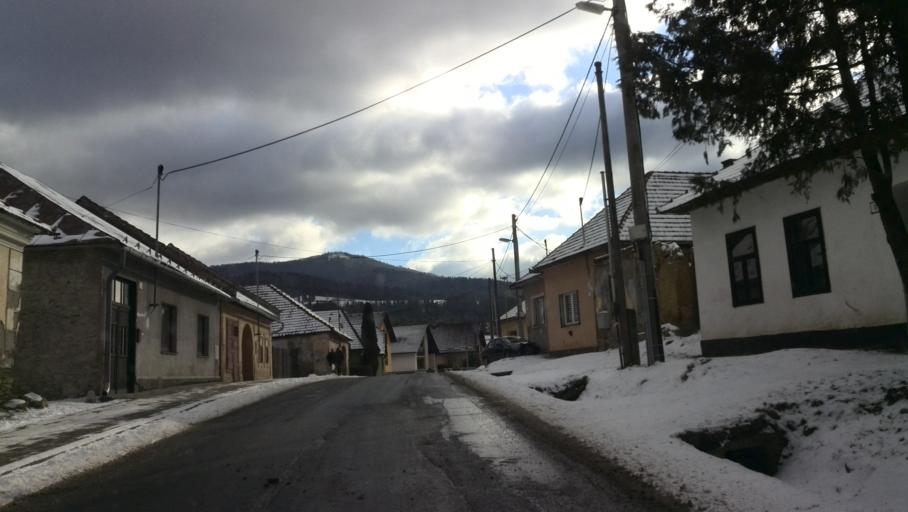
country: SK
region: Kosicky
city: Krompachy
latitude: 48.8036
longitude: 20.8056
